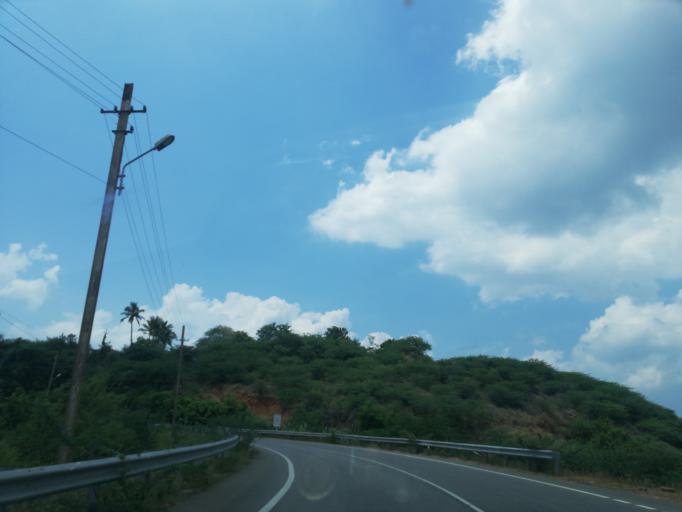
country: IN
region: Andhra Pradesh
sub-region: Guntur
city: Macherla
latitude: 16.6002
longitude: 79.3076
